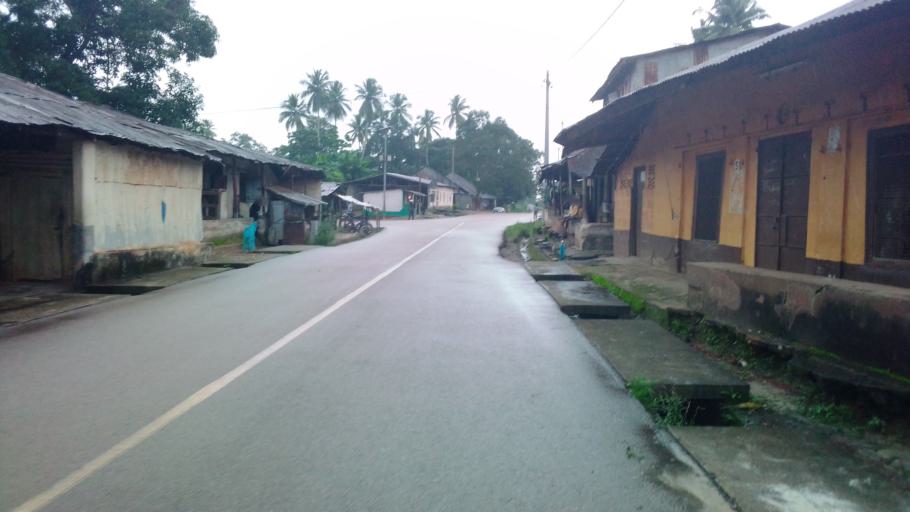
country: SL
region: Northern Province
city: Lunsar
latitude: 8.6796
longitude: -12.5330
